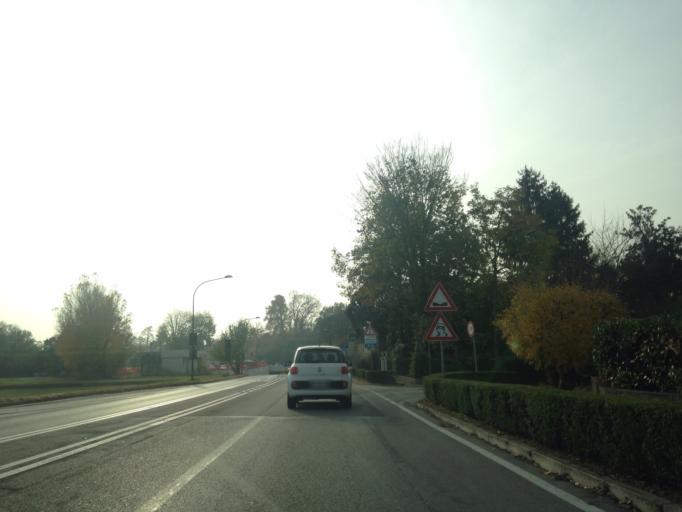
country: IT
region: Veneto
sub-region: Provincia di Treviso
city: Oderzo
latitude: 45.7767
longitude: 12.4916
